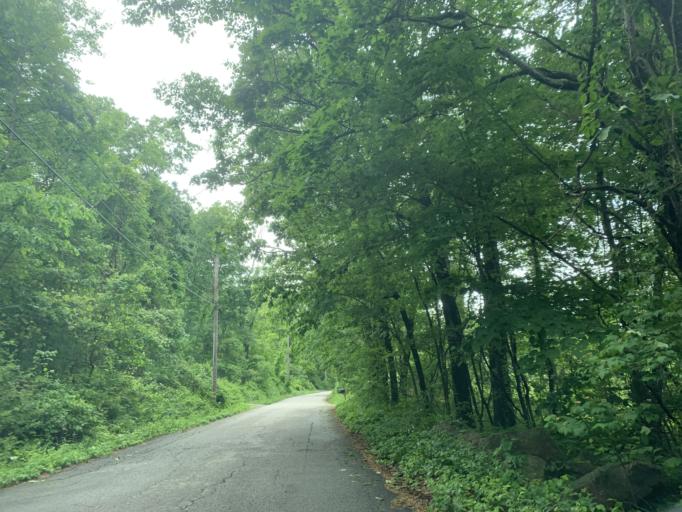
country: US
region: Massachusetts
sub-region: Worcester County
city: Upton
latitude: 42.1956
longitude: -71.6318
